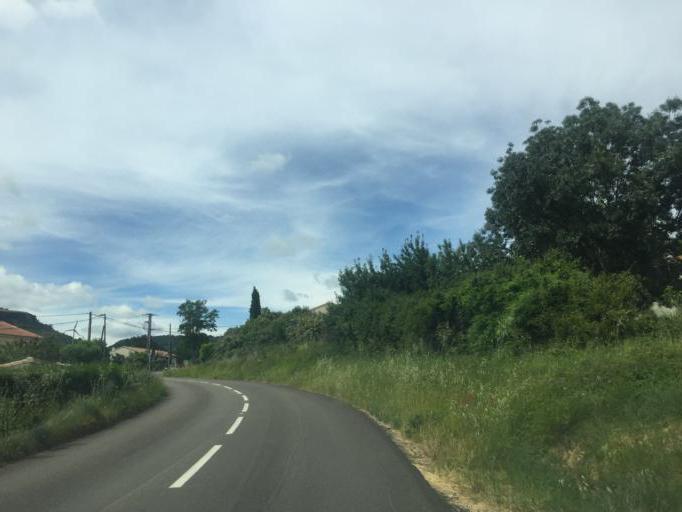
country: FR
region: Rhone-Alpes
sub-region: Departement de l'Ardeche
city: Villeneuve-de-Berg
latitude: 44.5974
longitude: 4.5374
